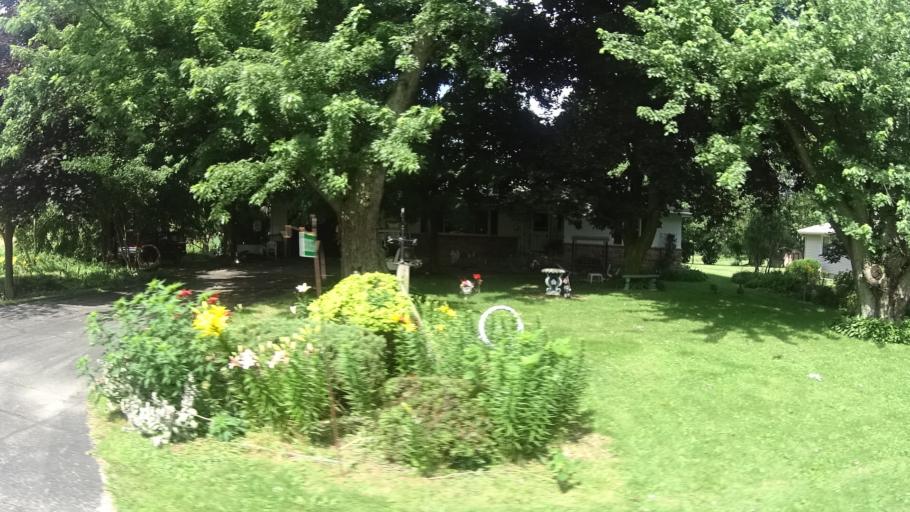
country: US
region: Ohio
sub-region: Huron County
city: Wakeman
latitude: 41.3170
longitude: -82.4137
